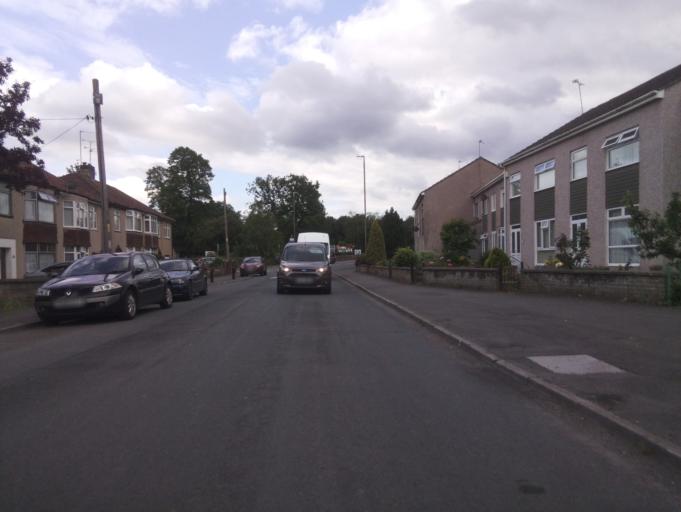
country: GB
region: England
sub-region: South Gloucestershire
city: Kingswood
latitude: 51.4575
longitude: -2.4871
